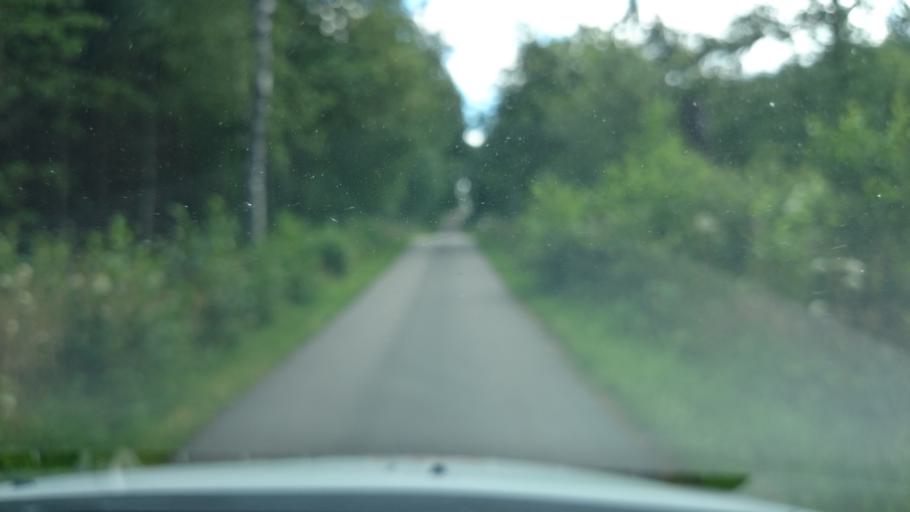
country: SE
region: Halland
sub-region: Hylte Kommun
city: Torup
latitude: 56.9562
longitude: 13.0932
